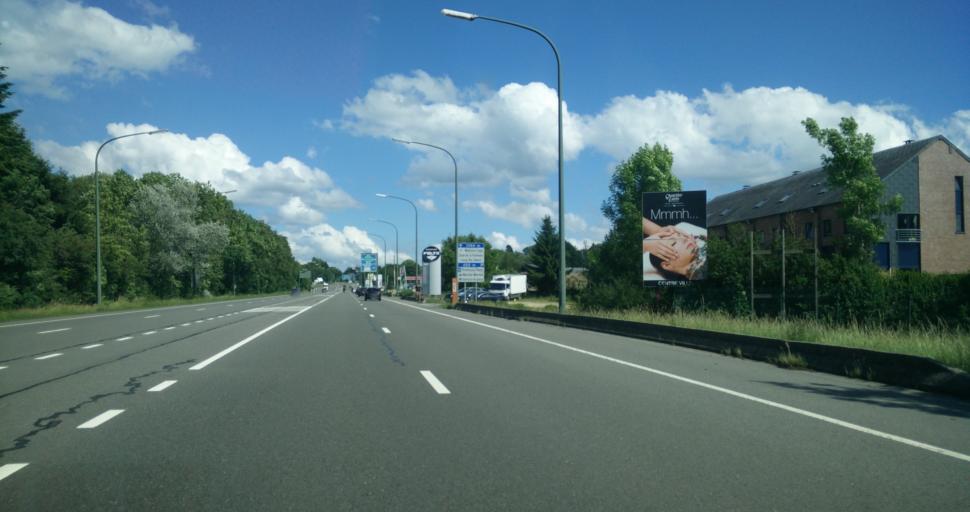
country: BE
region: Wallonia
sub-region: Province du Luxembourg
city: Marche-en-Famenne
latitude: 50.2315
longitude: 5.3210
